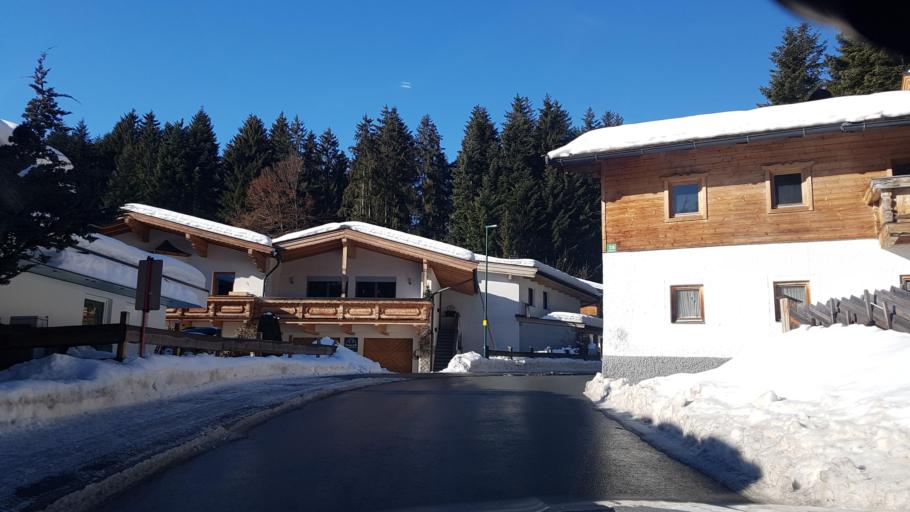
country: AT
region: Tyrol
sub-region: Politischer Bezirk Kitzbuhel
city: Oberndorf in Tirol
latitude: 47.5043
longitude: 12.3811
